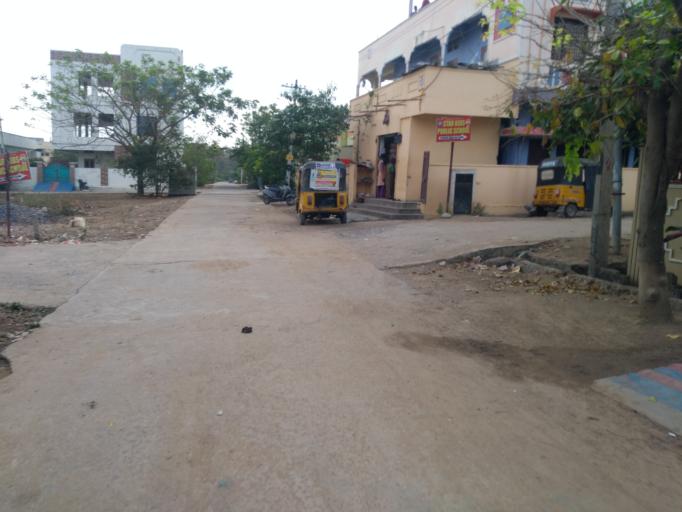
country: IN
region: Telangana
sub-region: Warangal
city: Warangal
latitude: 17.9523
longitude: 79.6016
